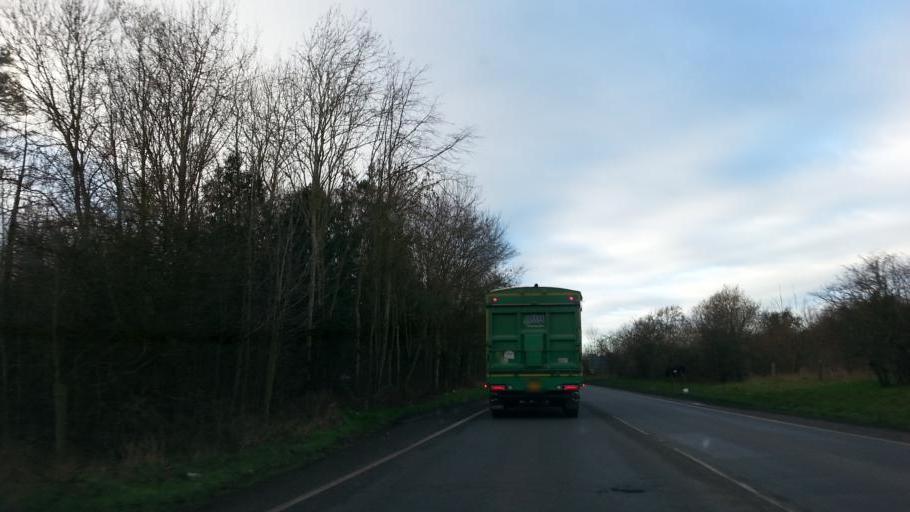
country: GB
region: England
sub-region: Suffolk
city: Bury St Edmunds
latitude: 52.2538
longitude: 0.7405
